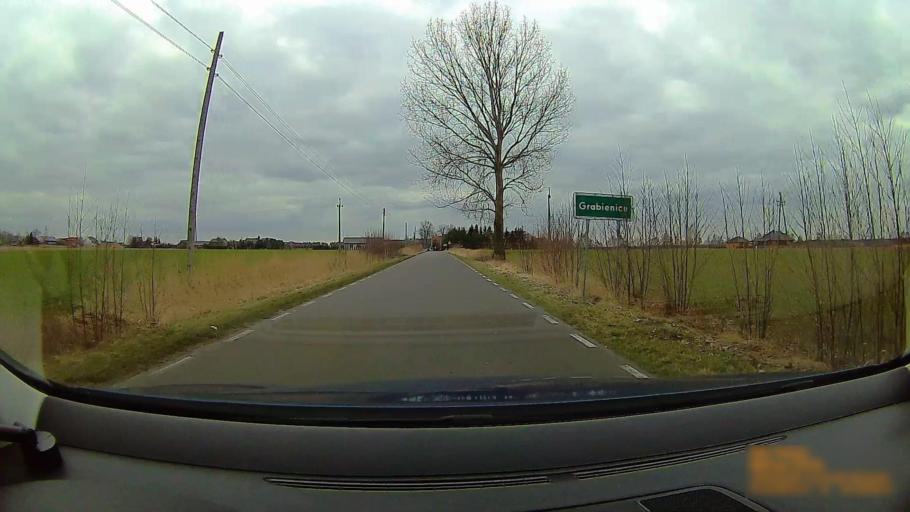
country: PL
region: Greater Poland Voivodeship
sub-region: Powiat koninski
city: Rzgow Pierwszy
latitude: 52.1375
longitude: 18.0568
